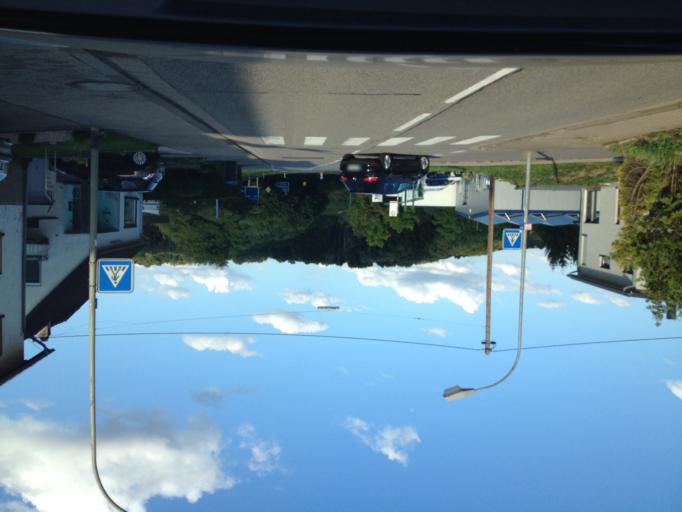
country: DE
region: Saarland
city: Tholey
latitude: 49.4881
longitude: 6.9835
